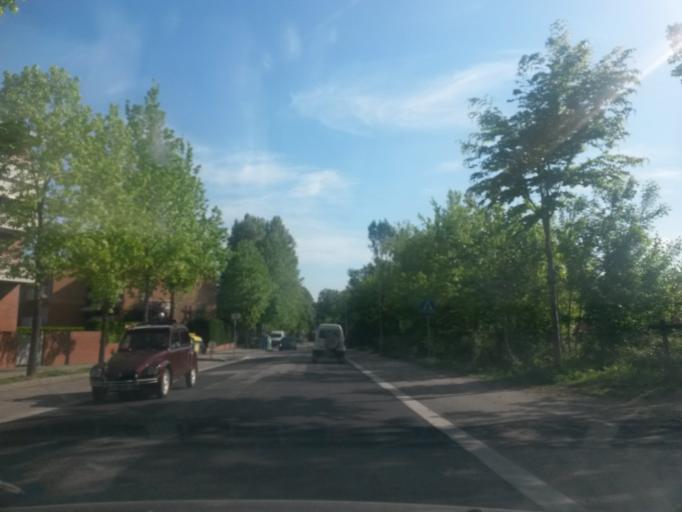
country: ES
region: Catalonia
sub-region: Provincia de Girona
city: Olot
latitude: 42.1720
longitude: 2.4861
